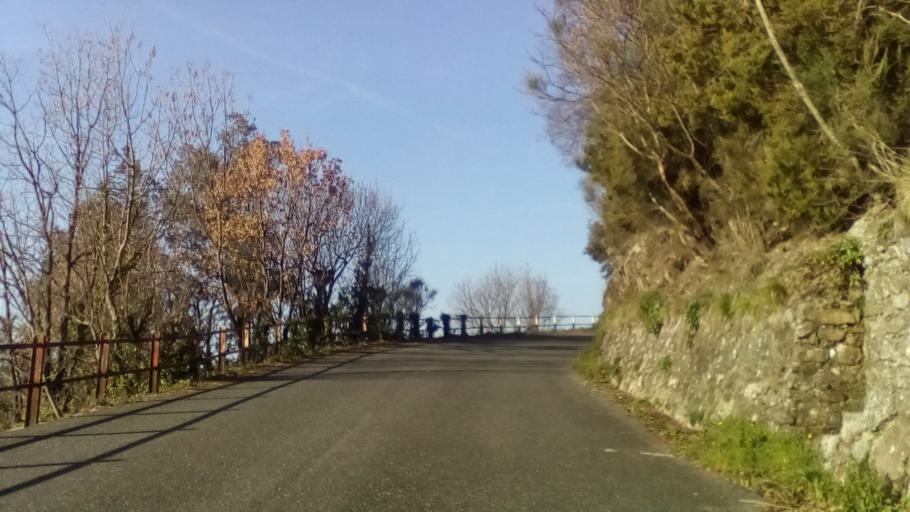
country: IT
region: Tuscany
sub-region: Provincia di Massa-Carrara
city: Montignoso
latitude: 44.0569
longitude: 10.1901
